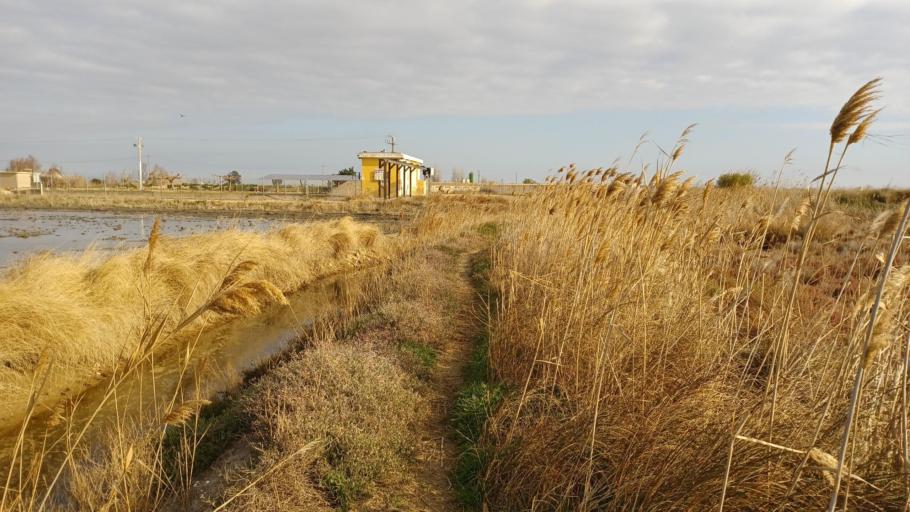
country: ES
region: Catalonia
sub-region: Provincia de Tarragona
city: Deltebre
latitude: 40.6381
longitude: 0.7110
